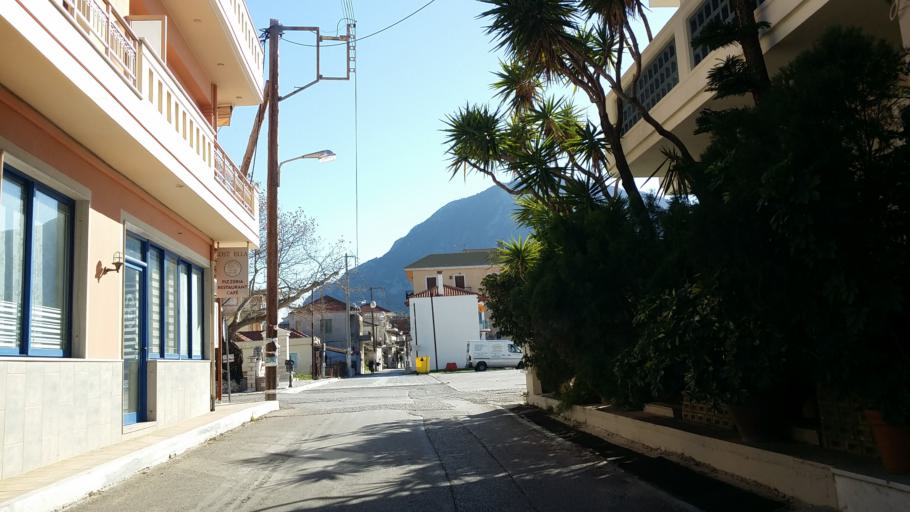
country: GR
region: West Greece
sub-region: Nomos Aitolias kai Akarnanias
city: Kandila
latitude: 38.6707
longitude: 20.9429
